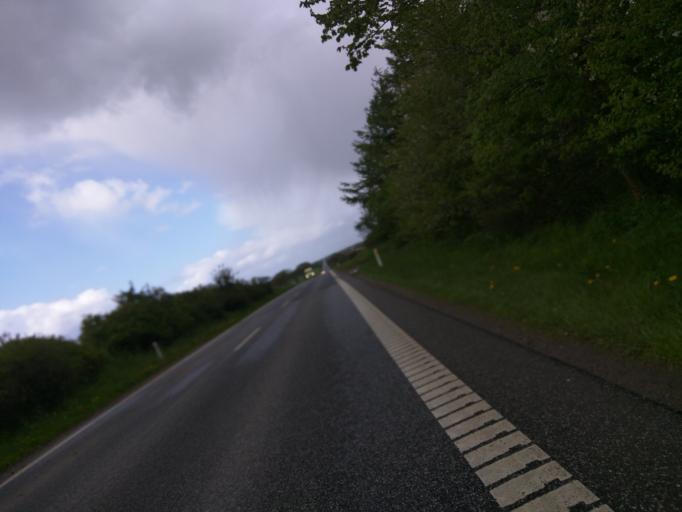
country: DK
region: Central Jutland
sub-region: Silkeborg Kommune
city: Kjellerup
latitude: 56.3561
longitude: 9.4357
